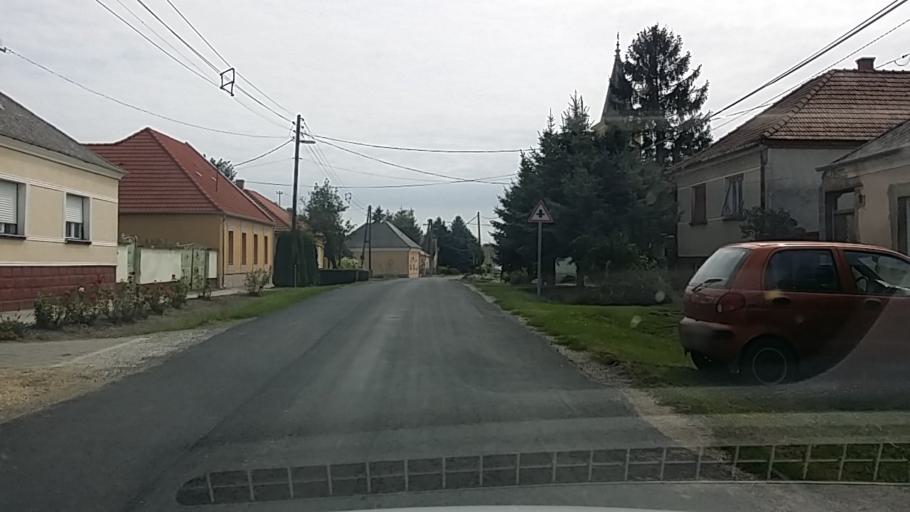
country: HU
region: Gyor-Moson-Sopron
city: Bosarkany
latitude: 47.7230
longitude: 17.3089
